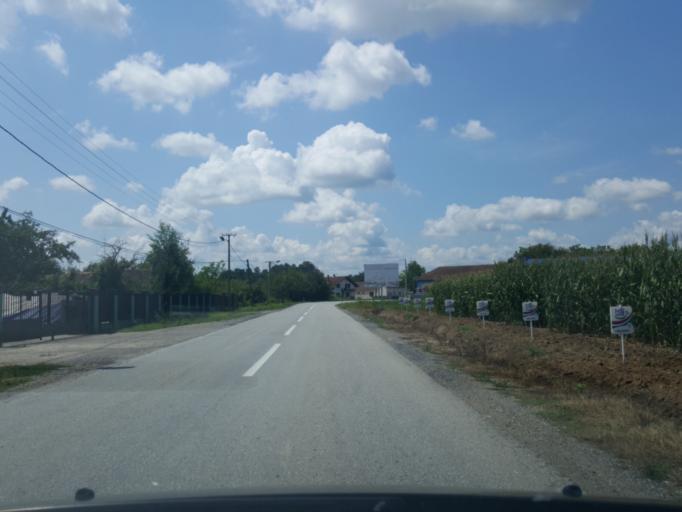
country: RS
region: Central Serbia
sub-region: Macvanski Okrug
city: Bogatic
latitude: 44.8415
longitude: 19.5145
